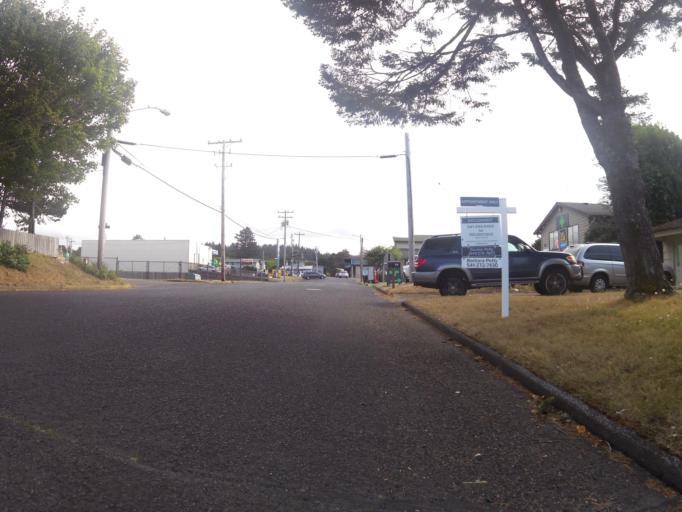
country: US
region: Oregon
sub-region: Lincoln County
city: Newport
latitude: 44.6482
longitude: -124.0547
